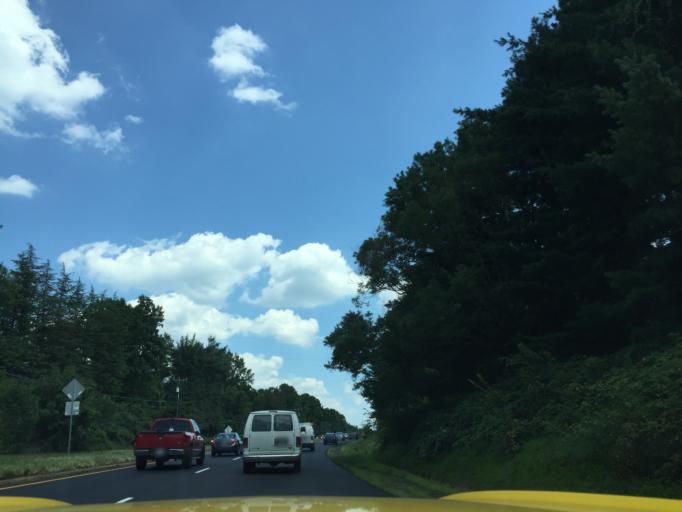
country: US
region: Virginia
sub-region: Fairfax County
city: Wolf Trap
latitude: 38.9647
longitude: -77.2844
